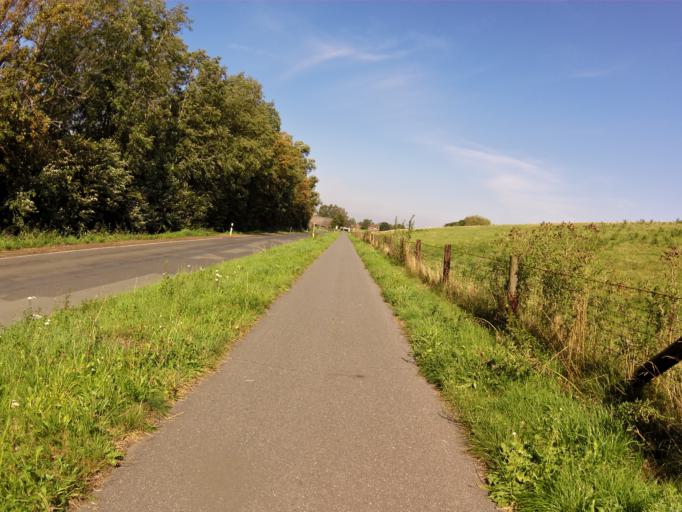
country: DE
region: Lower Saxony
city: Brake (Unterweser)
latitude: 53.2841
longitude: 8.4823
